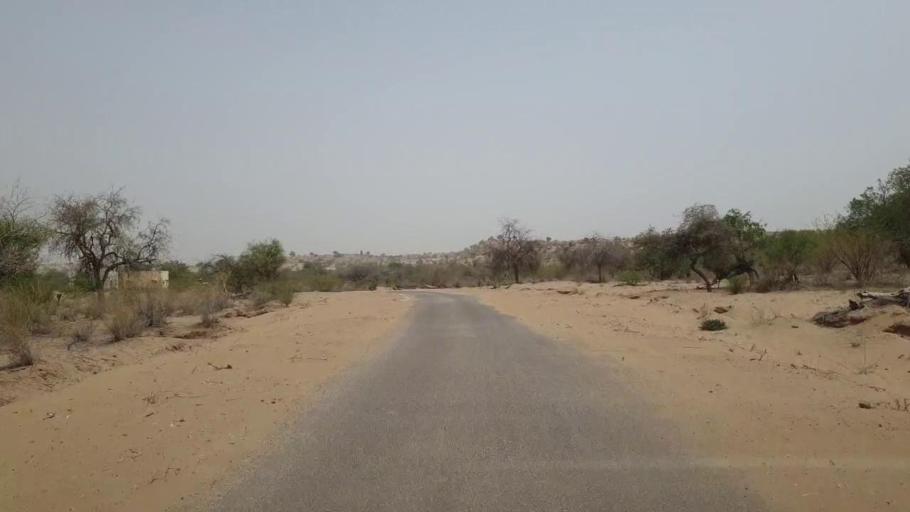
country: PK
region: Sindh
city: Islamkot
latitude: 24.7979
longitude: 70.5401
